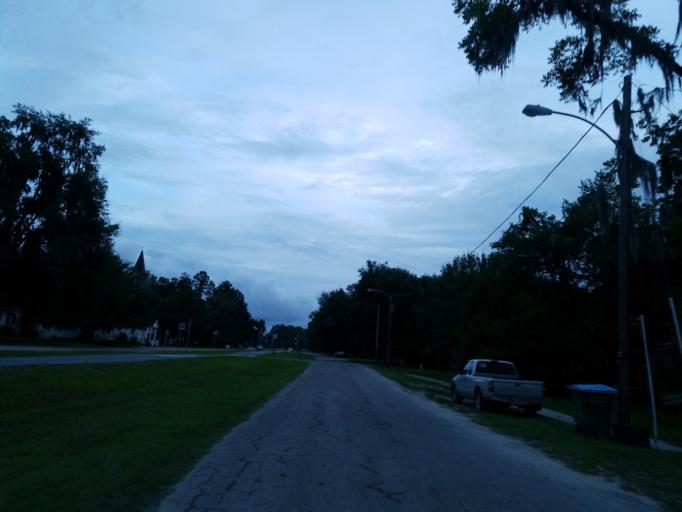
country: US
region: Florida
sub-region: Hamilton County
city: Jasper
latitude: 30.5159
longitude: -82.9480
